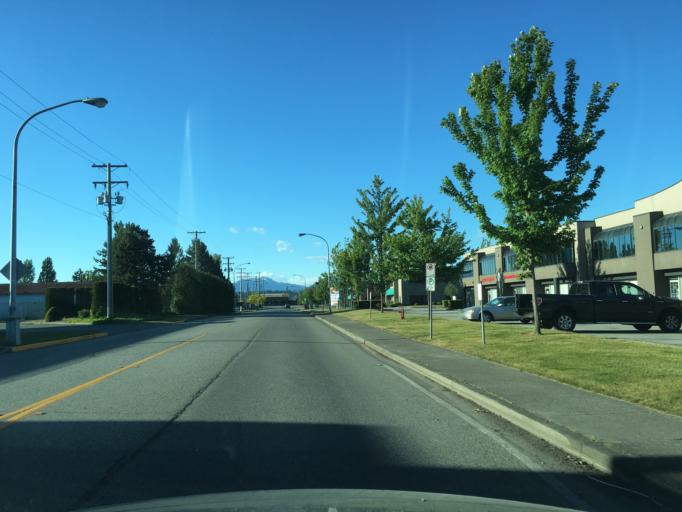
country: CA
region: British Columbia
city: Delta
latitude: 49.1664
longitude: -122.9898
